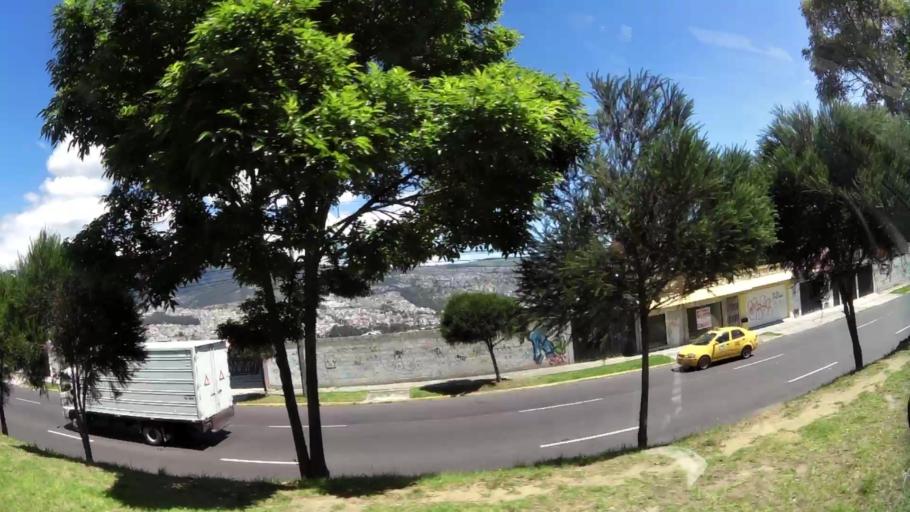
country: EC
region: Pichincha
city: Quito
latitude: -0.0998
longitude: -78.4832
